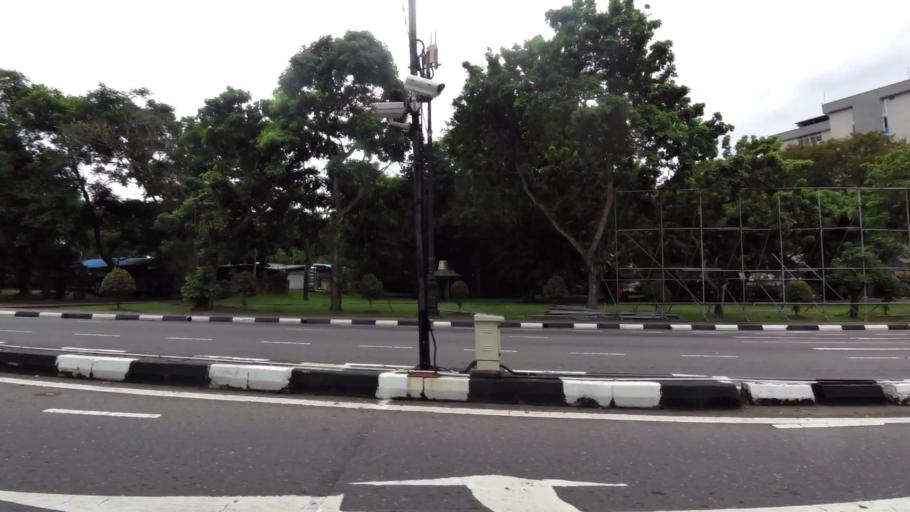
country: BN
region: Brunei and Muara
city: Bandar Seri Begawan
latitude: 4.8943
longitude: 114.9406
